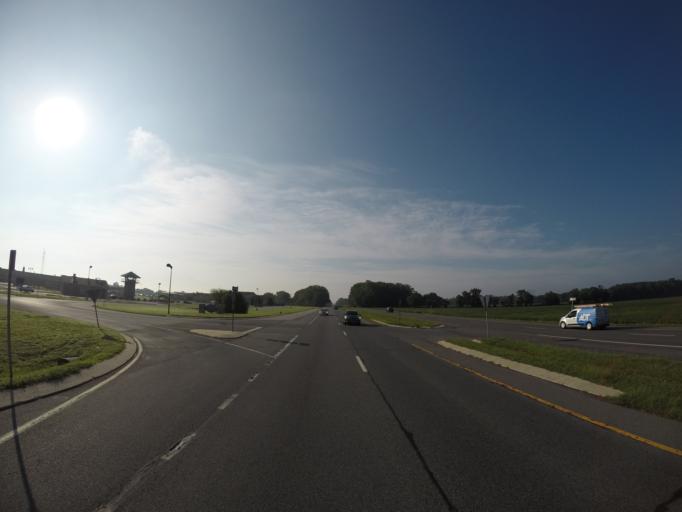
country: US
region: Delaware
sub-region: Sussex County
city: Georgetown
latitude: 38.6595
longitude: -75.3742
